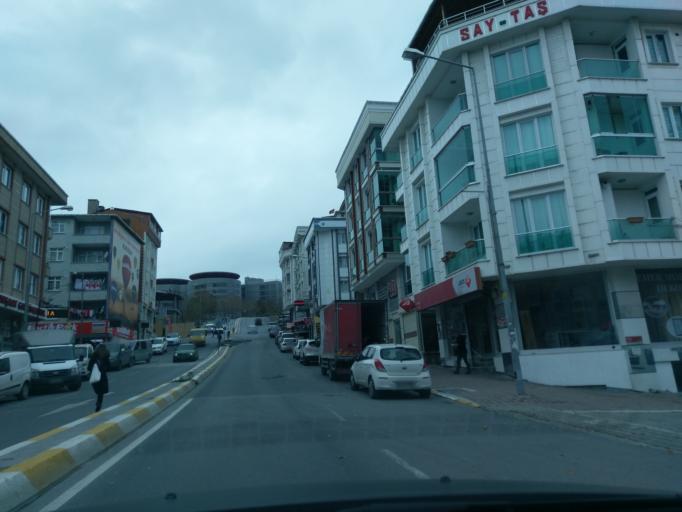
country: TR
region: Istanbul
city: Esenyurt
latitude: 41.0106
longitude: 28.6648
